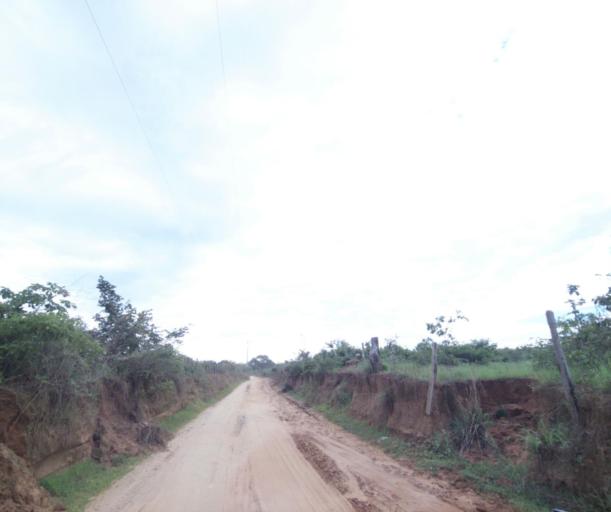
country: BR
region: Bahia
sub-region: Carinhanha
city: Carinhanha
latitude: -14.1808
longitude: -44.5209
